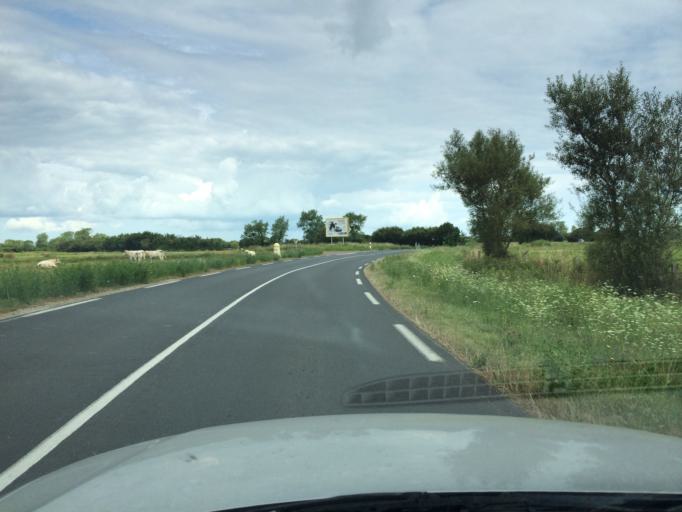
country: FR
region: Lower Normandy
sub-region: Departement de la Manche
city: Saint-Hilaire-Petitville
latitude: 49.3994
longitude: -1.2000
